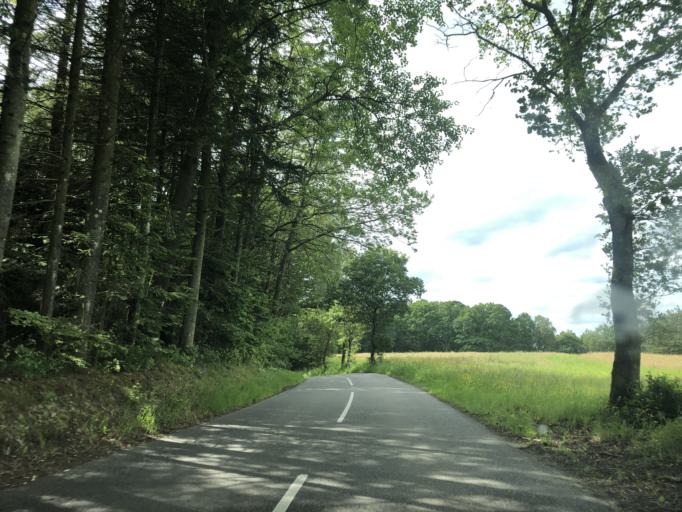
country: DK
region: Central Jutland
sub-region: Silkeborg Kommune
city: Svejbaek
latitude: 56.2221
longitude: 9.6931
